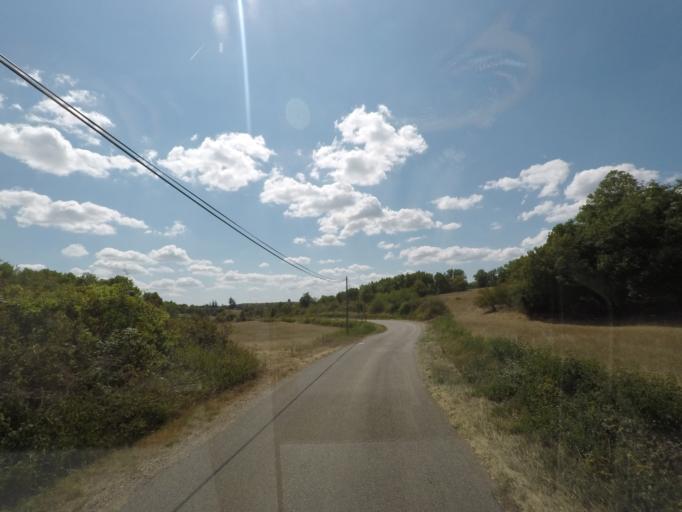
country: FR
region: Midi-Pyrenees
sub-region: Departement du Lot
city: Cajarc
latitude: 44.5534
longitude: 1.6733
